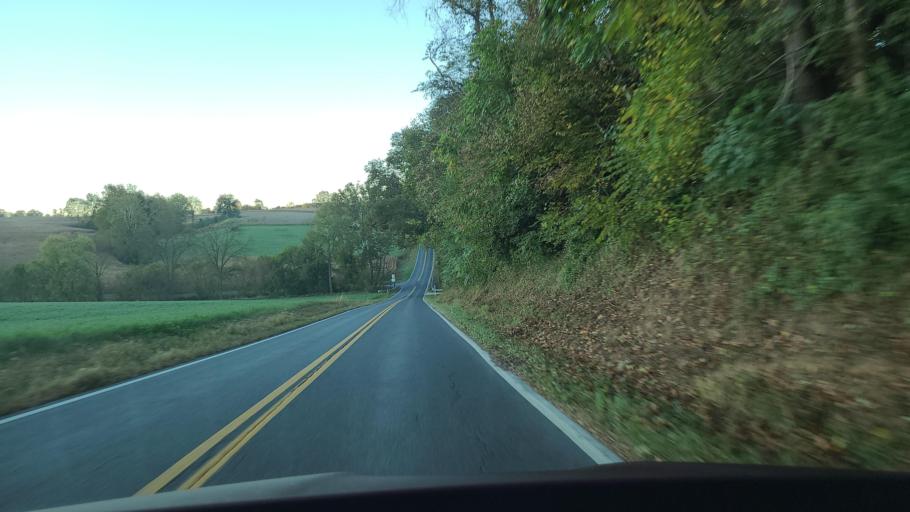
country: US
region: Maryland
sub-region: Frederick County
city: Jefferson
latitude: 39.3796
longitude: -77.5377
